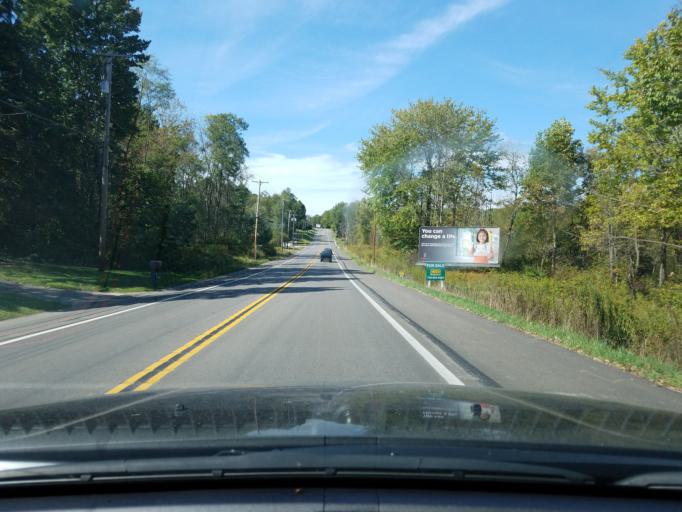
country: US
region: Pennsylvania
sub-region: Lawrence County
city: New Castle
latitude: 40.9563
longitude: -80.2865
